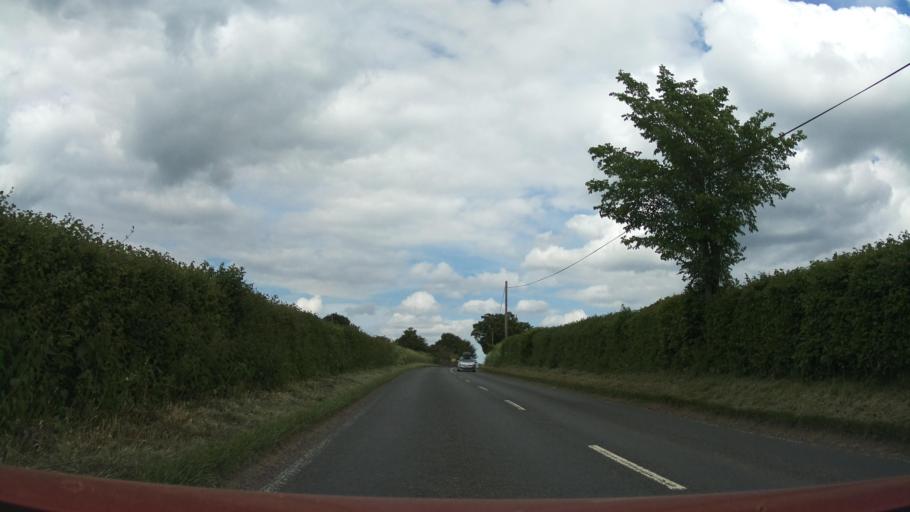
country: GB
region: England
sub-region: Herefordshire
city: Yatton
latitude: 51.9487
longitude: -2.5458
